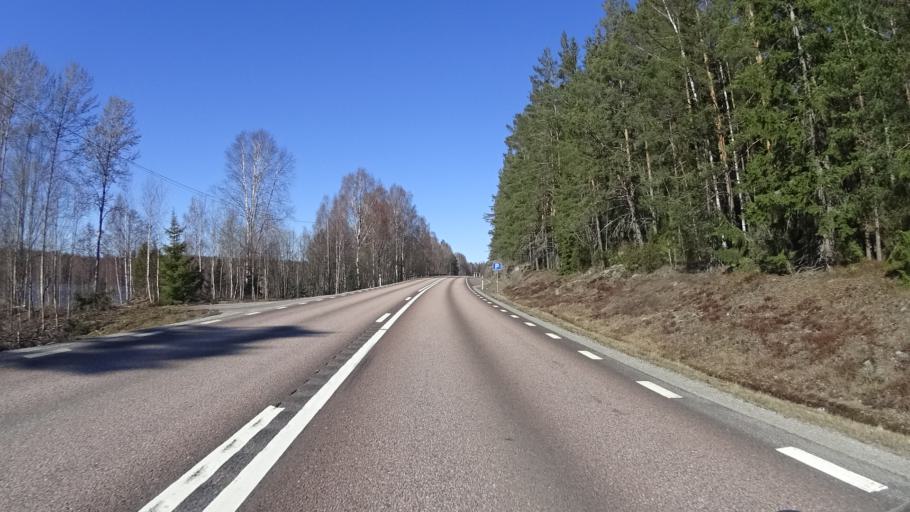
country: SE
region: Vaermland
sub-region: Sunne Kommun
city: Sunne
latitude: 59.6444
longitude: 12.9444
